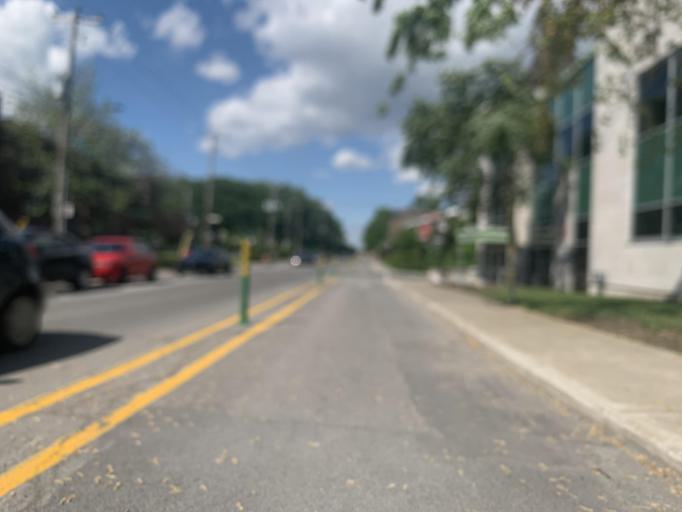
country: CA
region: Quebec
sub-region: Montreal
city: Saint-Leonard
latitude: 45.5562
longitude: -73.5804
